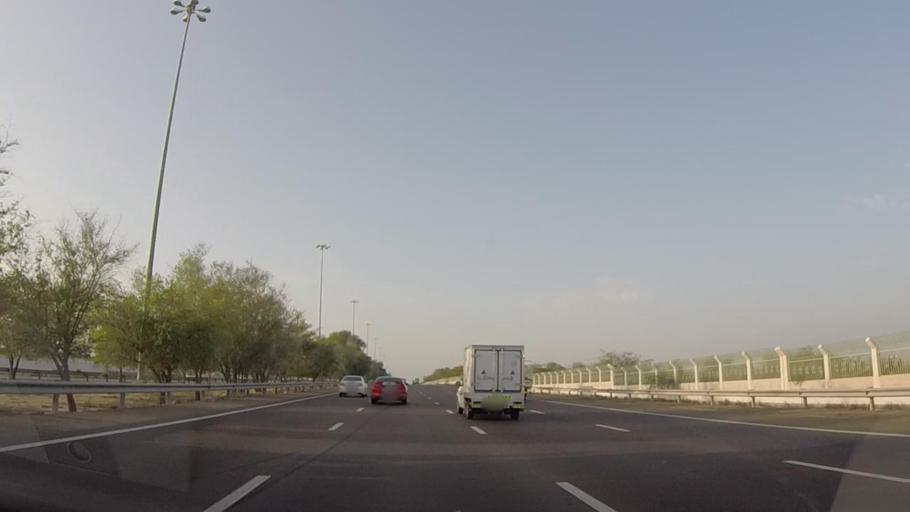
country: AE
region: Dubai
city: Dubai
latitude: 24.8298
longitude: 54.8822
